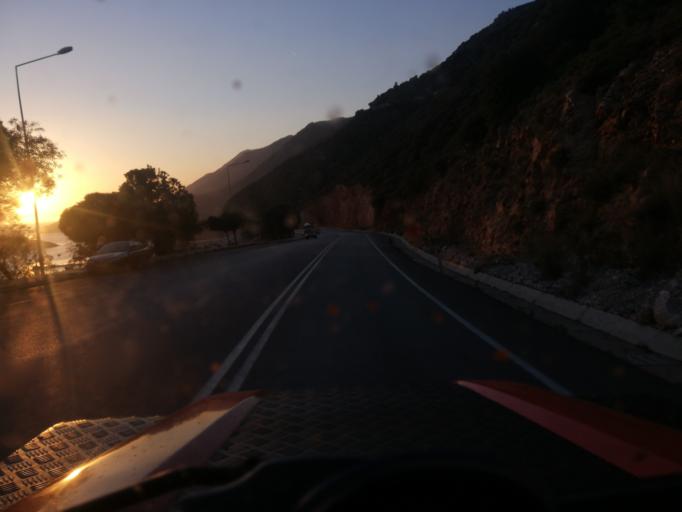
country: TR
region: Antalya
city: Kas
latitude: 36.2058
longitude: 29.6361
